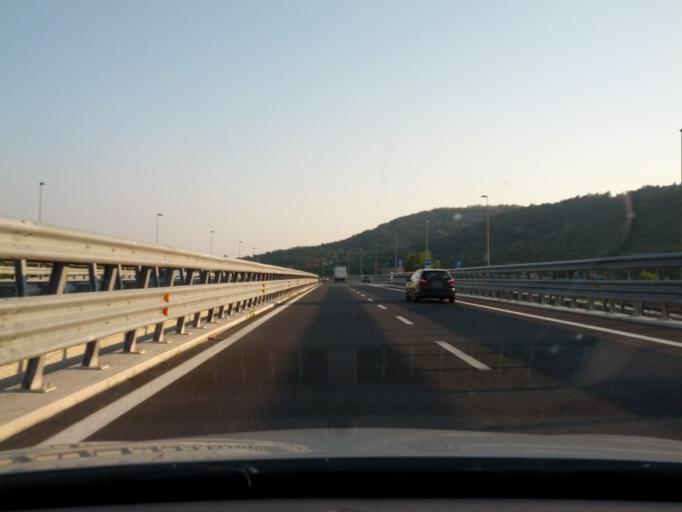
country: SI
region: Koper-Capodistria
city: Spodnje Skofije
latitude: 45.5903
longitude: 13.7997
